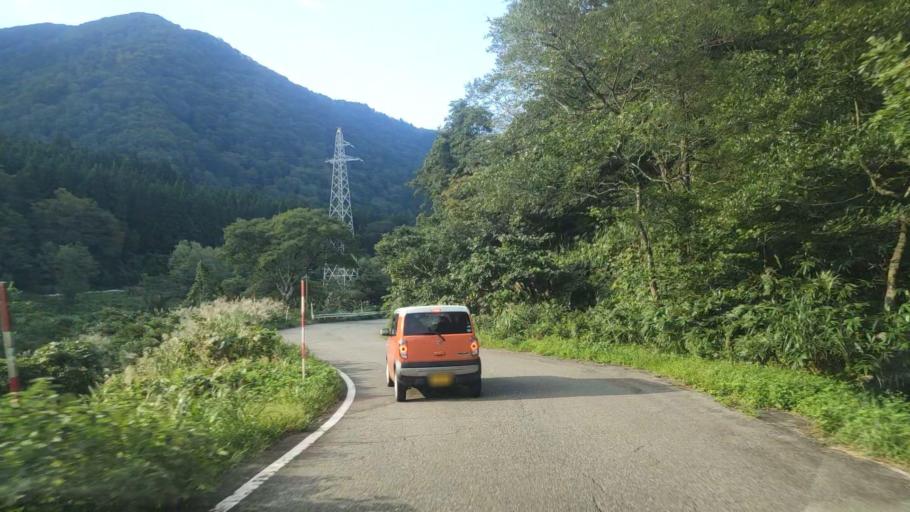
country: JP
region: Toyama
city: Yatsuomachi-higashikumisaka
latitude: 36.4525
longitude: 137.0848
